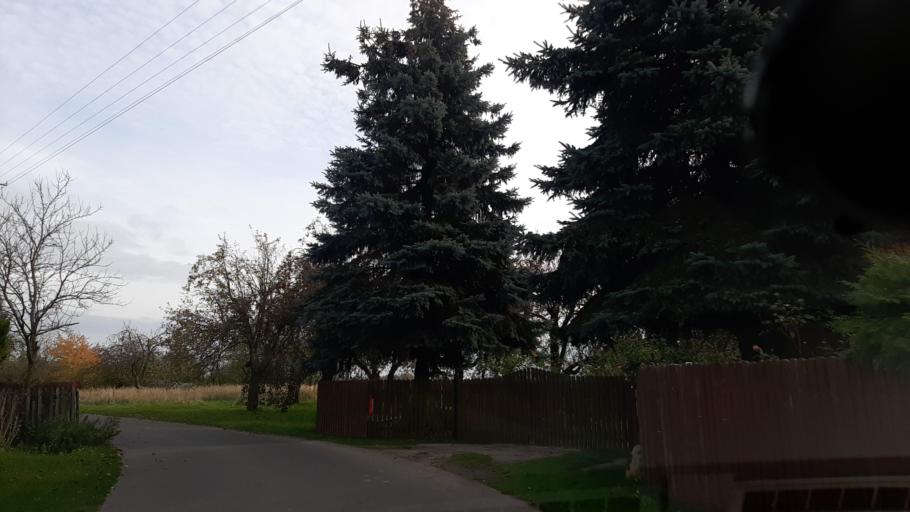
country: PL
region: Lublin Voivodeship
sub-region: Powiat lubelski
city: Garbow
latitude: 51.4099
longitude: 22.3873
